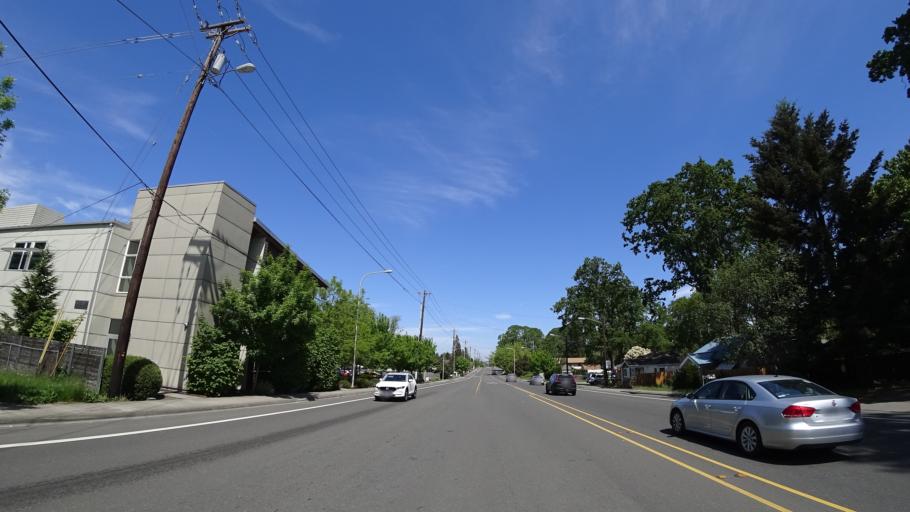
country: US
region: Oregon
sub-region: Washington County
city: Aloha
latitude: 45.4863
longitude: -122.8673
